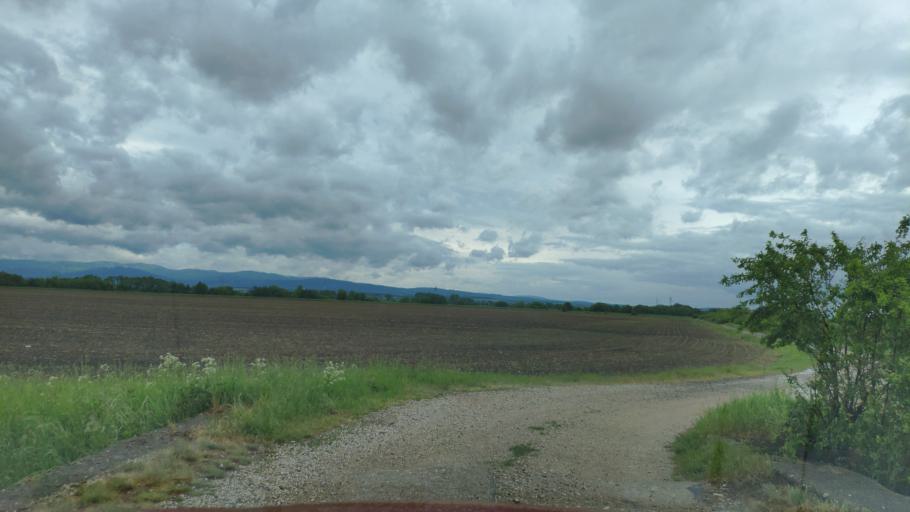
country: SK
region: Kosicky
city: Moldava nad Bodvou
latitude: 48.5512
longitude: 21.1137
